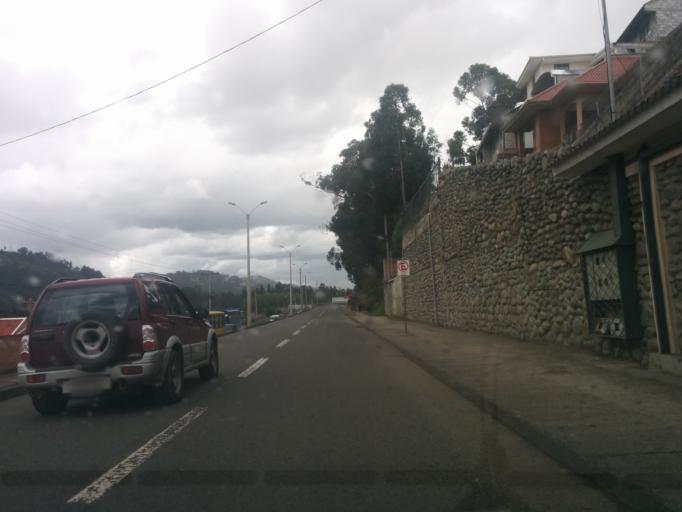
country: EC
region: Azuay
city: Cuenca
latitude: -2.8884
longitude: -78.9609
